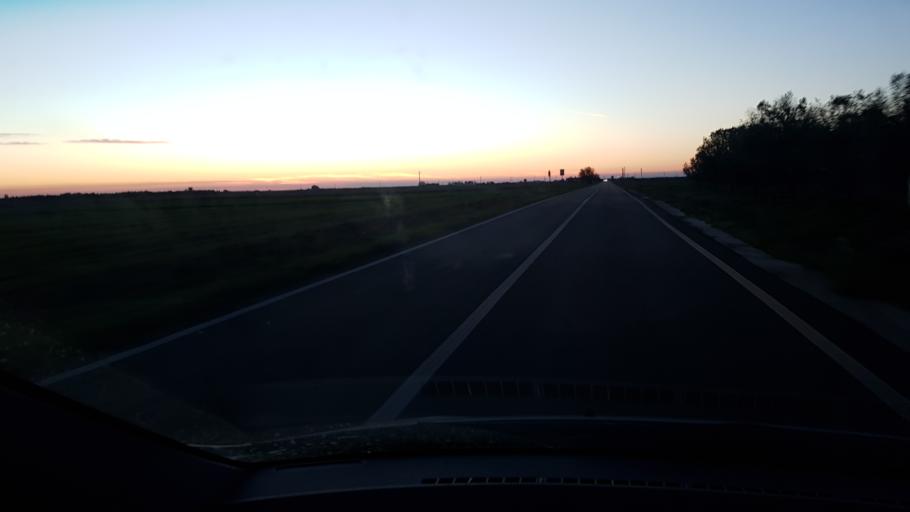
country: IT
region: Apulia
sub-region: Provincia di Brindisi
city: Tuturano
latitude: 40.5281
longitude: 17.9060
